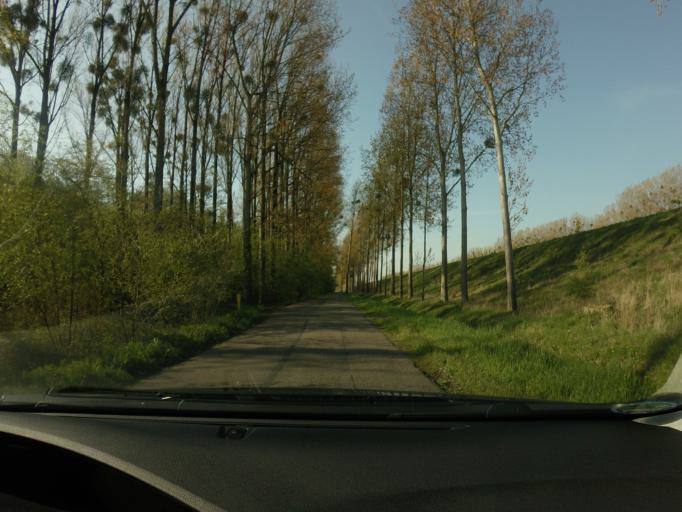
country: NL
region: Limburg
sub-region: Gemeente Stein
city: Elsloo
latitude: 50.9366
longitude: 5.7498
